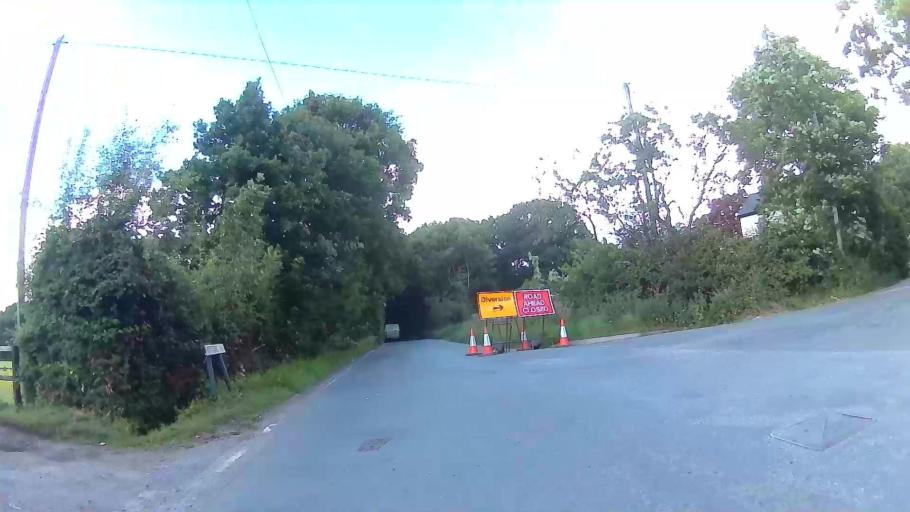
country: GB
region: England
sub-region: Greater London
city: Collier Row
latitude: 51.6321
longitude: 0.1916
